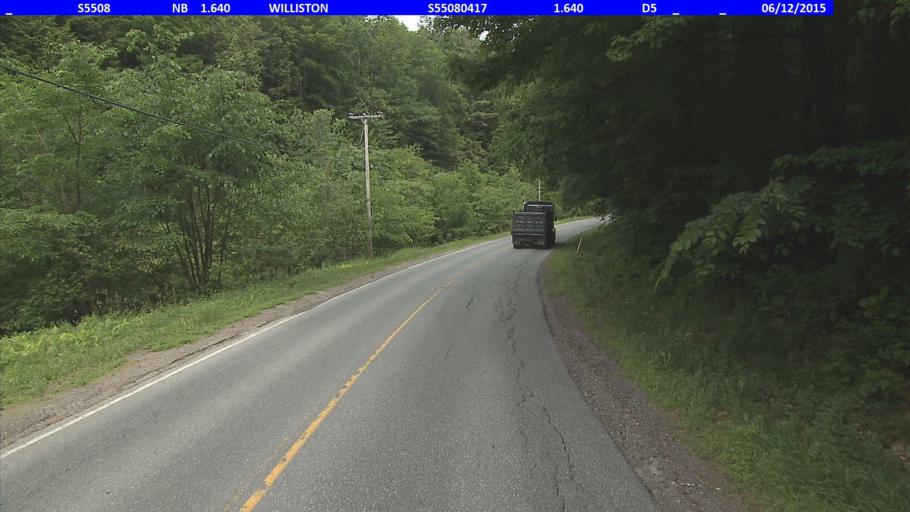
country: US
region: Vermont
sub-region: Chittenden County
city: Williston
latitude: 44.4580
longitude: -73.0564
